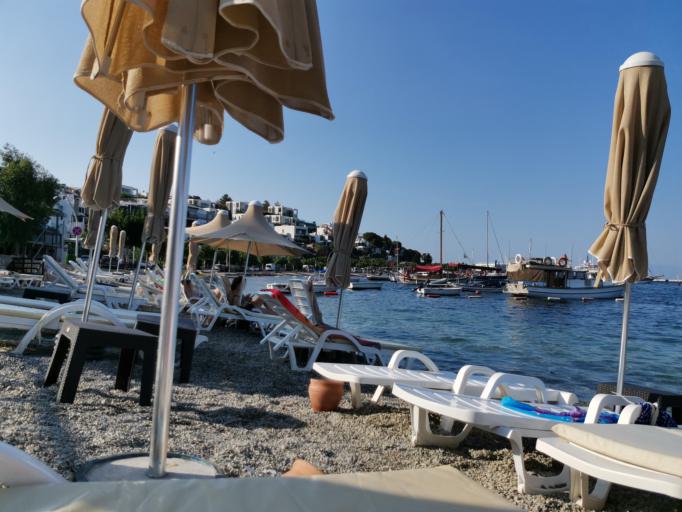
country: TR
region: Mugla
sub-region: Bodrum
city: Bodrum
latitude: 37.0281
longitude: 27.4408
